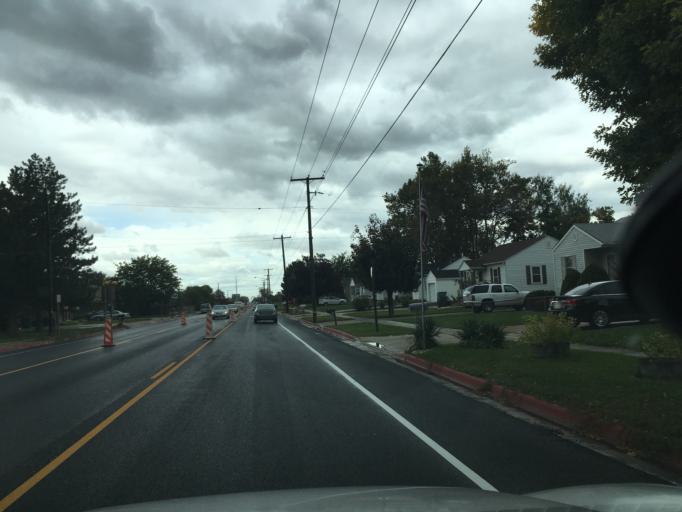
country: US
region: Utah
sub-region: Davis County
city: Layton
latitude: 41.0601
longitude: -111.9531
